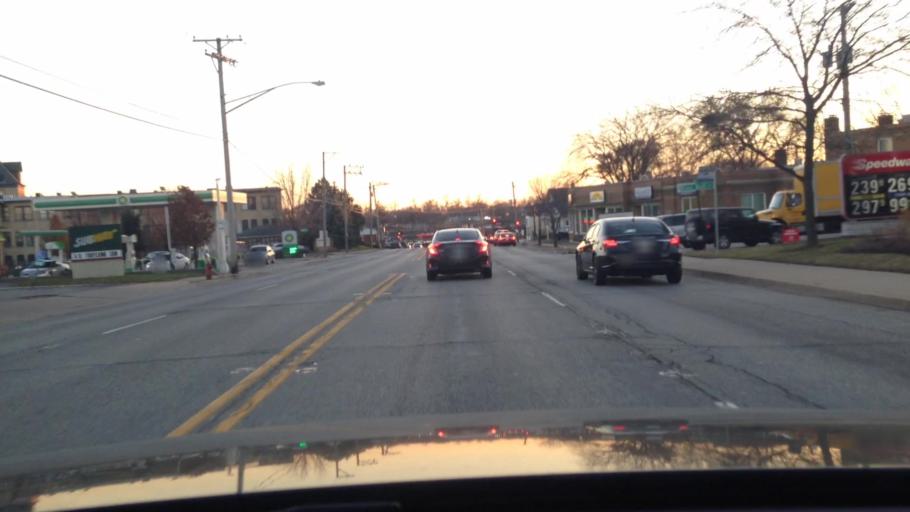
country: US
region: Illinois
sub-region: Kane County
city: Elgin
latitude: 42.0587
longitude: -88.2667
